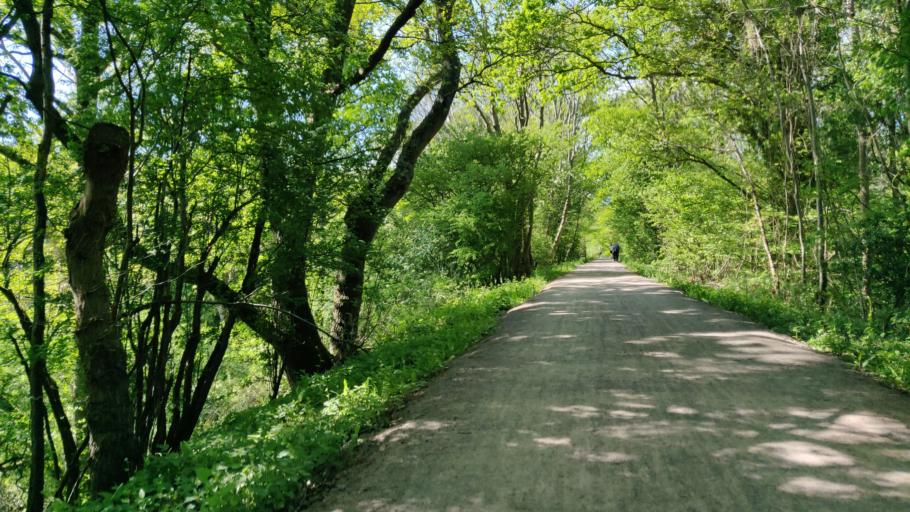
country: GB
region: England
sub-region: West Sussex
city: Rudgwick
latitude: 51.0847
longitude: -0.4427
